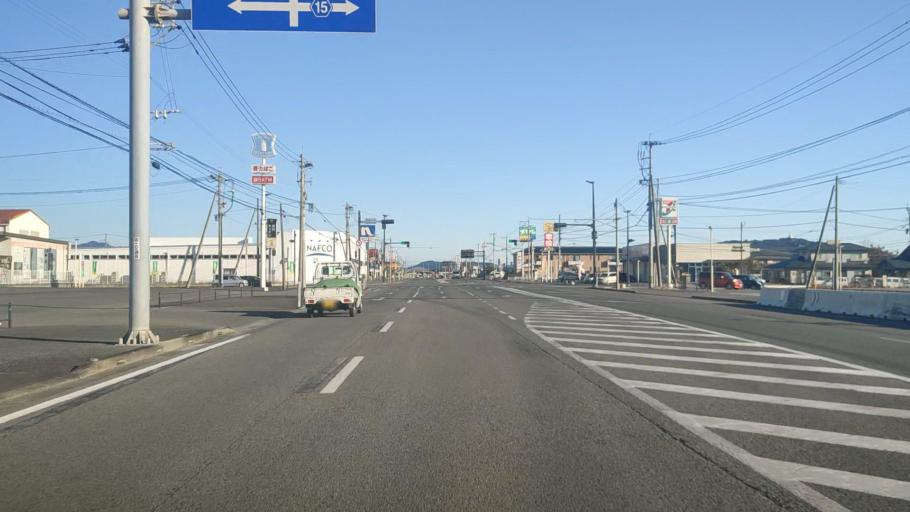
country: JP
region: Miyazaki
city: Nobeoka
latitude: 32.3961
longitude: 131.6292
